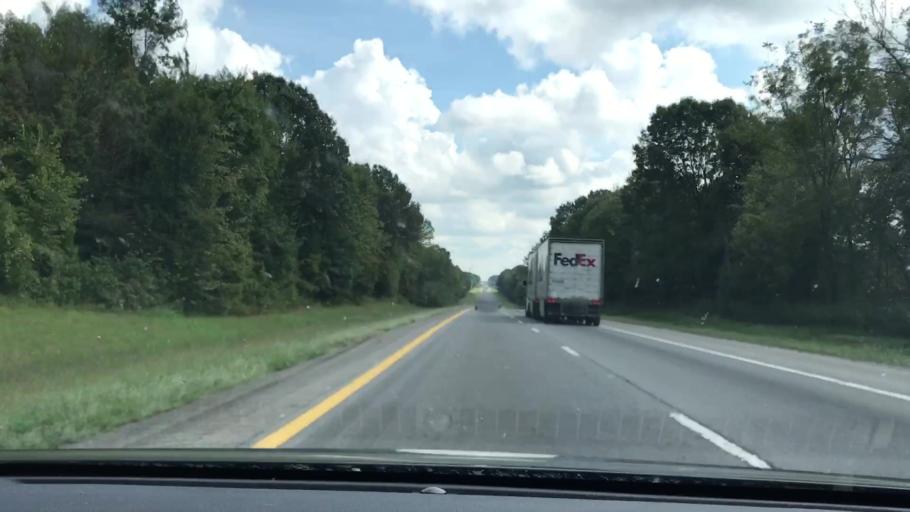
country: US
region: Tennessee
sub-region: Cheatham County
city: Pleasant View
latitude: 36.4607
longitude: -87.1160
